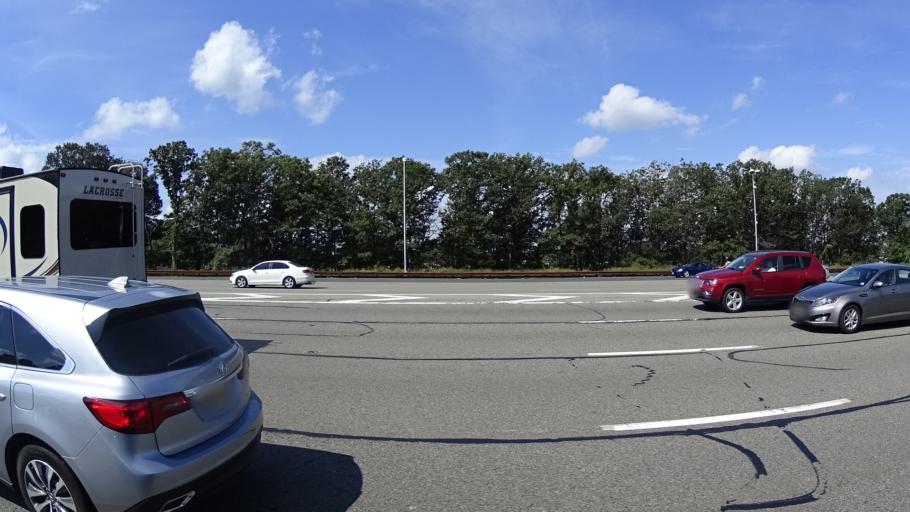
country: US
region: New Jersey
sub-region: Middlesex County
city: South Amboy
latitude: 40.4837
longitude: -74.3028
